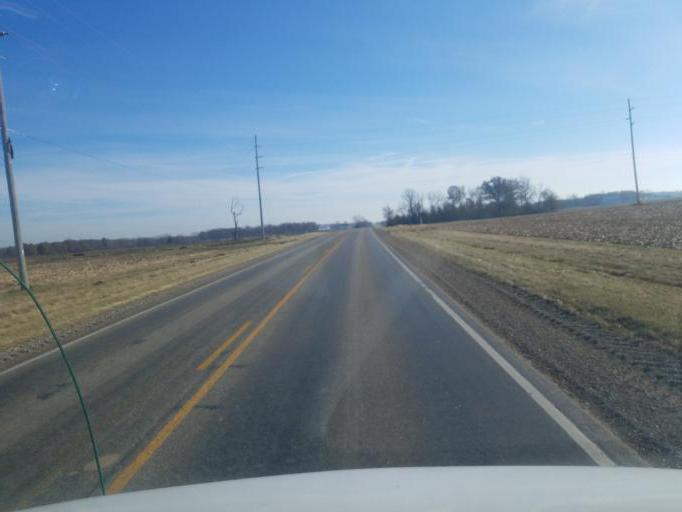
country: US
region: Indiana
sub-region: Adams County
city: Geneva
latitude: 40.5414
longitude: -84.9543
